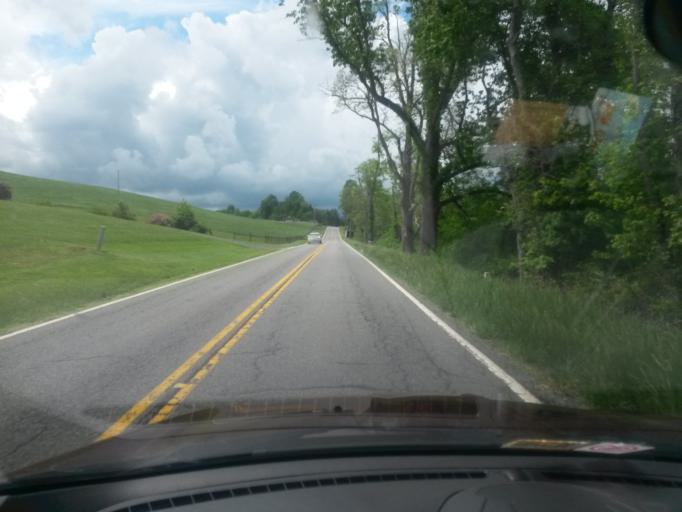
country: US
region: Virginia
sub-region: Floyd County
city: Floyd
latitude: 36.8613
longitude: -80.3251
